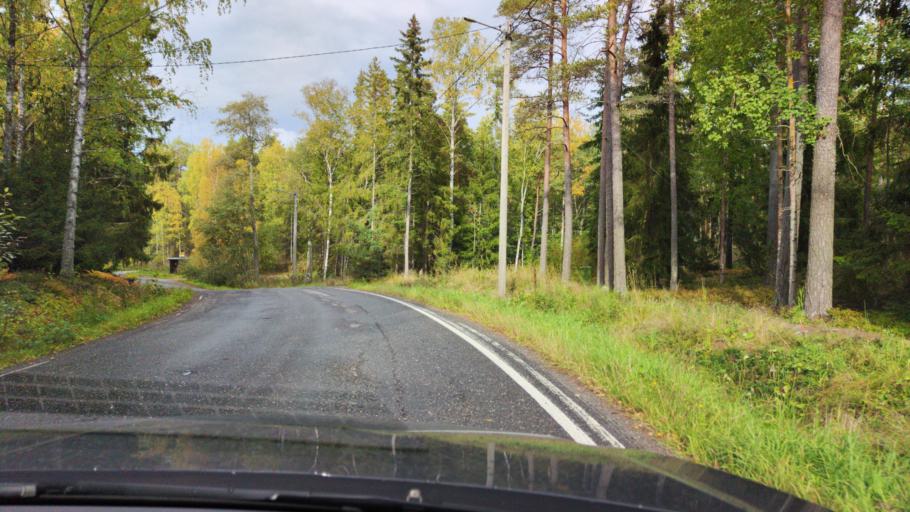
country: FI
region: Varsinais-Suomi
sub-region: Aboland-Turunmaa
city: Pargas
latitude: 60.3489
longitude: 22.1849
